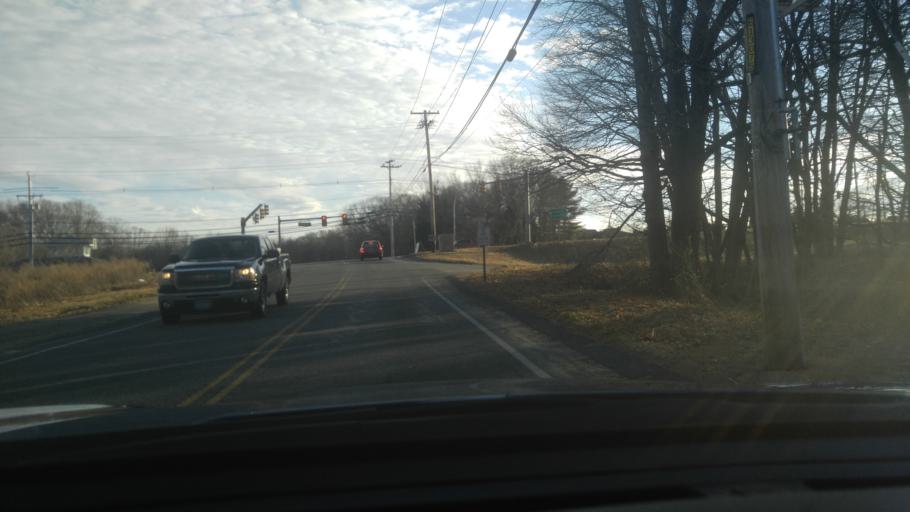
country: US
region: Rhode Island
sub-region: Washington County
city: Exeter
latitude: 41.5838
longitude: -71.4980
